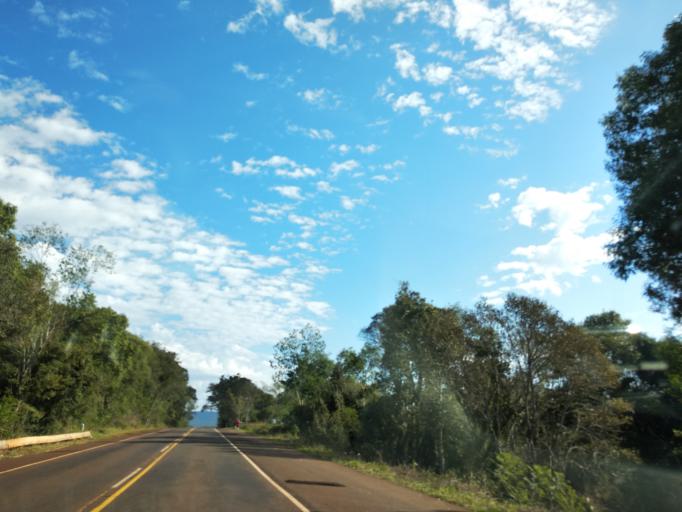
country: AR
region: Misiones
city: Aristobulo del Valle
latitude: -27.0967
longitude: -54.9562
